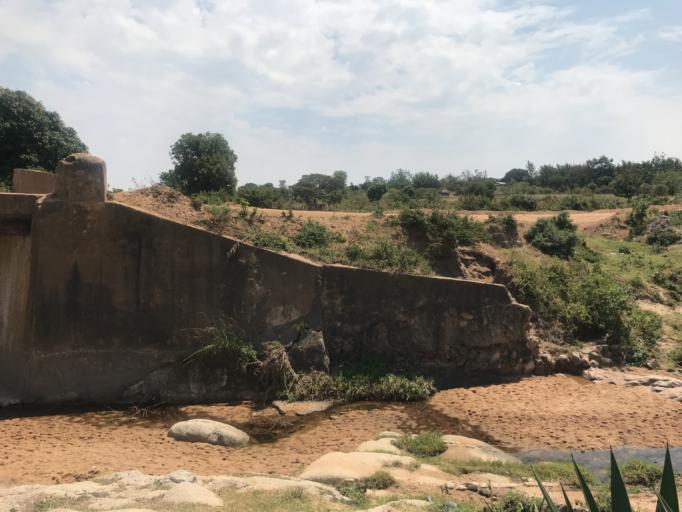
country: TZ
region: Mara
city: Nyamuswa
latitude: -1.9142
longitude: 34.0134
